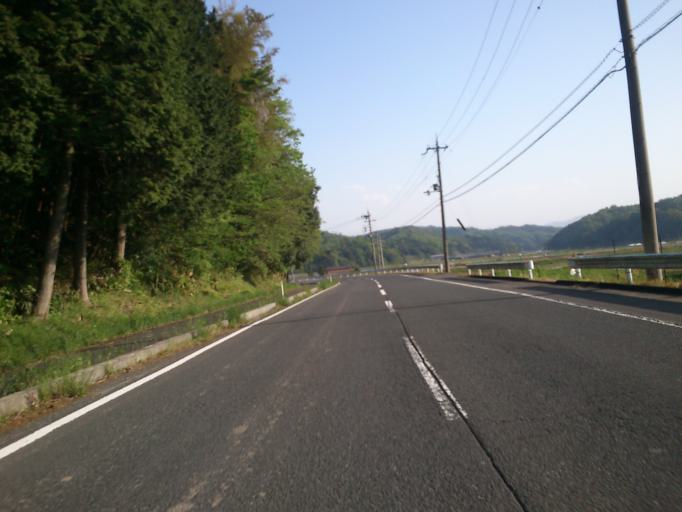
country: JP
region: Kyoto
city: Miyazu
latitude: 35.6004
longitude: 135.1392
